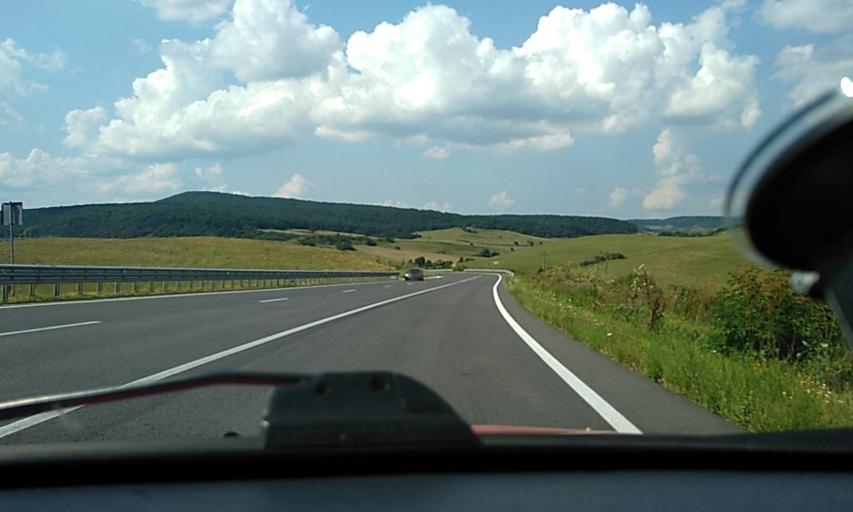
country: RO
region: Brasov
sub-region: Oras Rupea
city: Fiser
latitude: 46.0951
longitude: 25.1059
